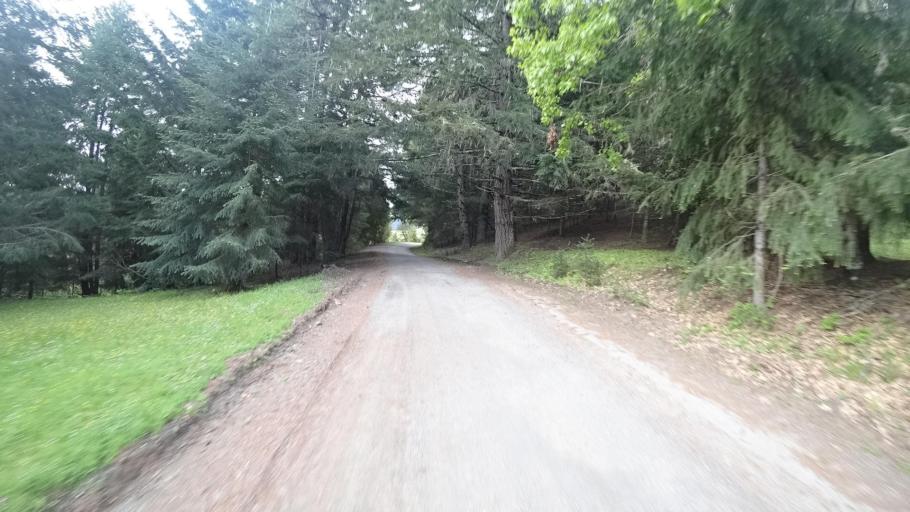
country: US
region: California
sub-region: Humboldt County
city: Redway
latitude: 40.2101
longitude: -123.6819
